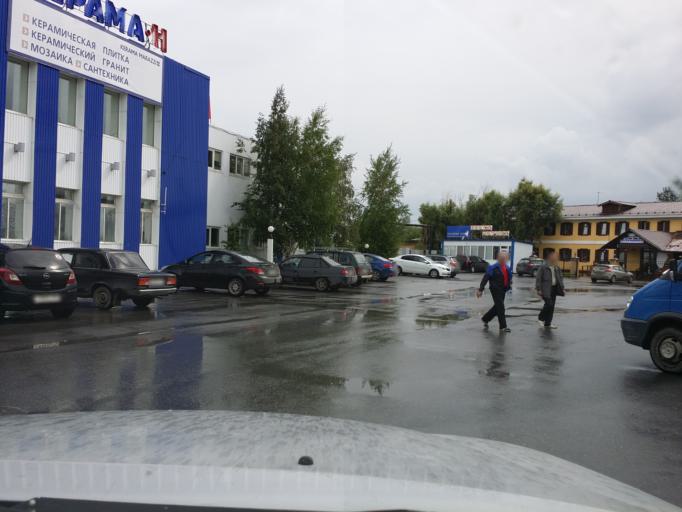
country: RU
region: Khanty-Mansiyskiy Avtonomnyy Okrug
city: Nizhnevartovsk
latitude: 60.9496
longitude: 76.4984
